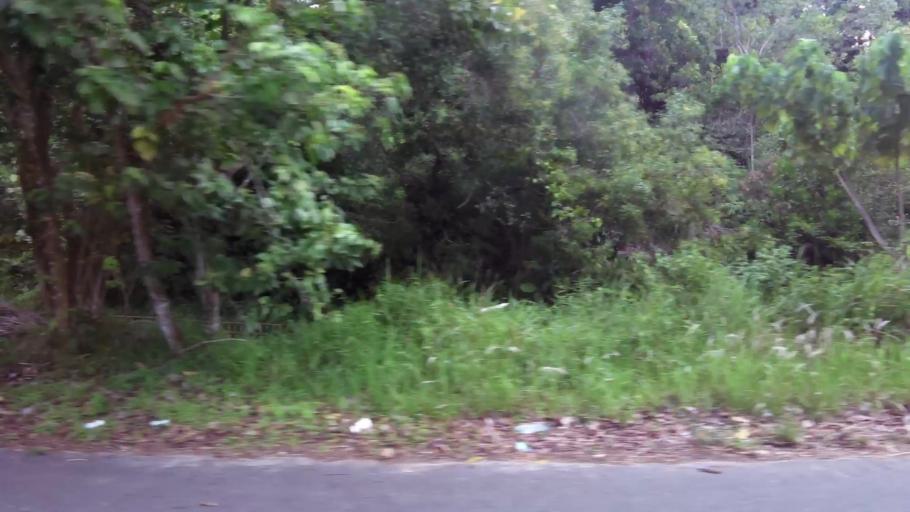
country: BN
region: Brunei and Muara
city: Bandar Seri Begawan
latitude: 4.9618
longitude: 114.9870
